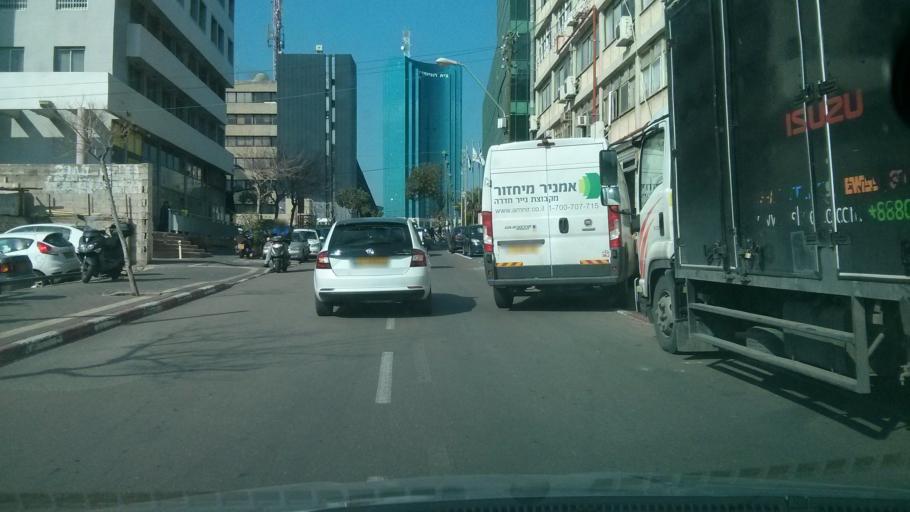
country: IL
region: Tel Aviv
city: Tel Aviv
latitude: 32.0638
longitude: 34.7882
